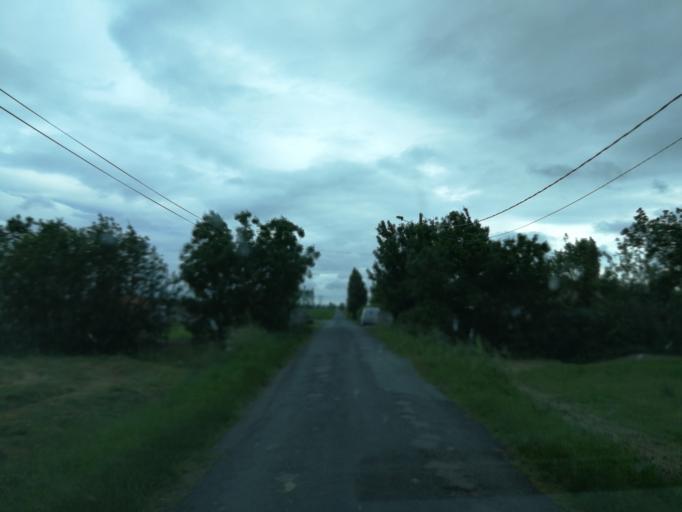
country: FR
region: Pays de la Loire
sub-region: Departement de la Vendee
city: Le Langon
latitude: 46.3728
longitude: -0.9302
